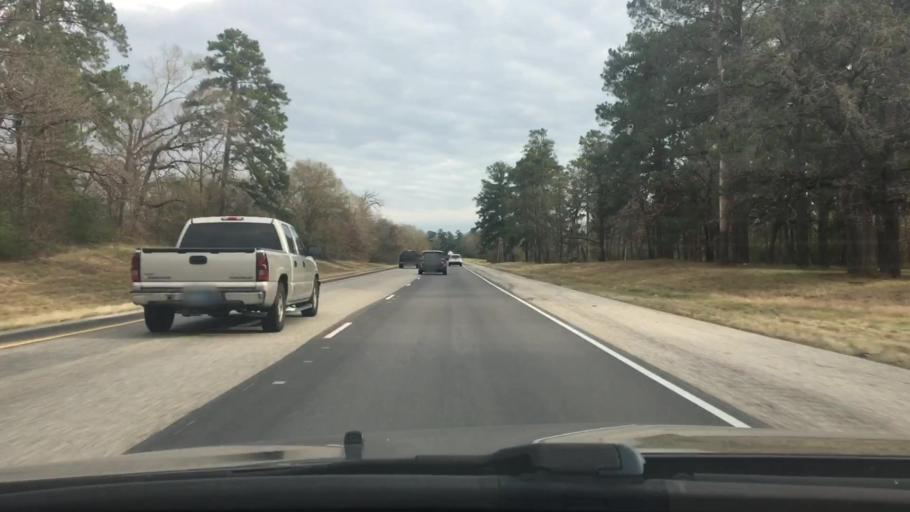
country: US
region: Texas
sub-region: Walker County
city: Huntsville
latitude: 30.7996
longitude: -95.6830
